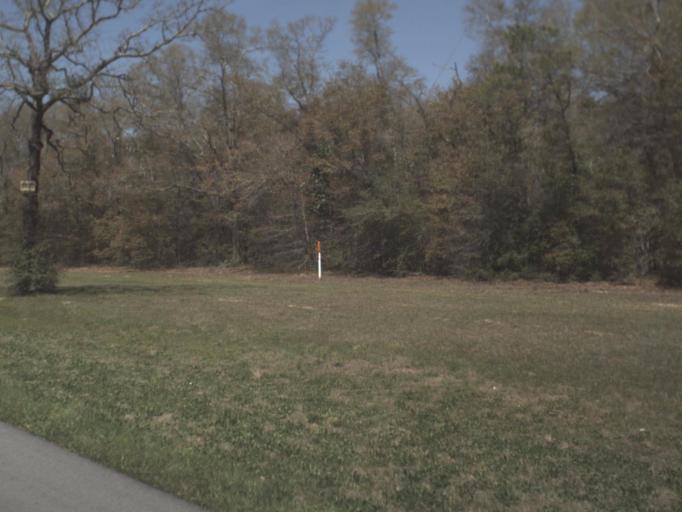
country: US
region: Florida
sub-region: Okaloosa County
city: Crestview
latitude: 30.7371
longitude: -86.3619
